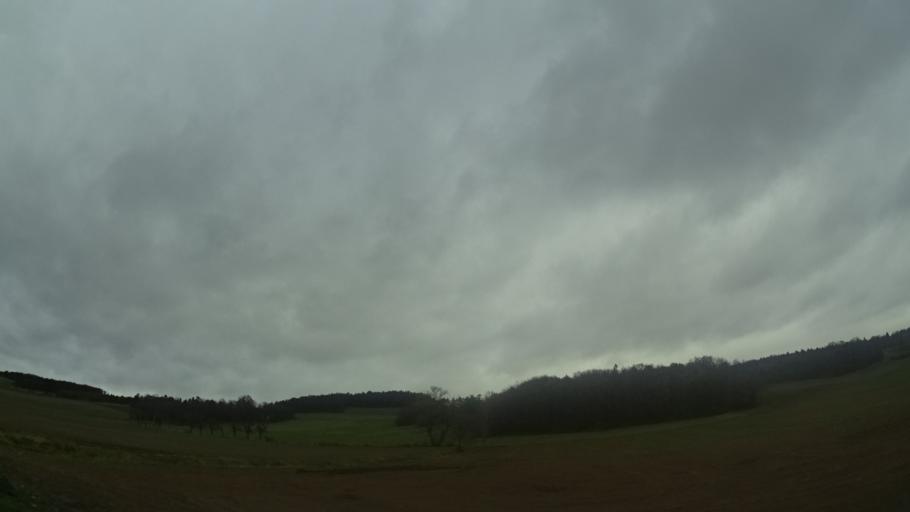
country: DE
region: Thuringia
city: Blankenhain
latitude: 50.8539
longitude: 11.3882
